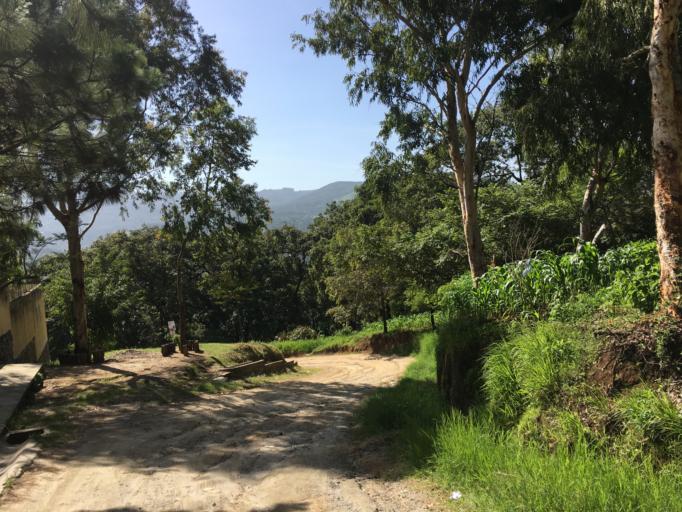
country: GT
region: Guatemala
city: Villa Canales
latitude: 14.4839
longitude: -90.5436
